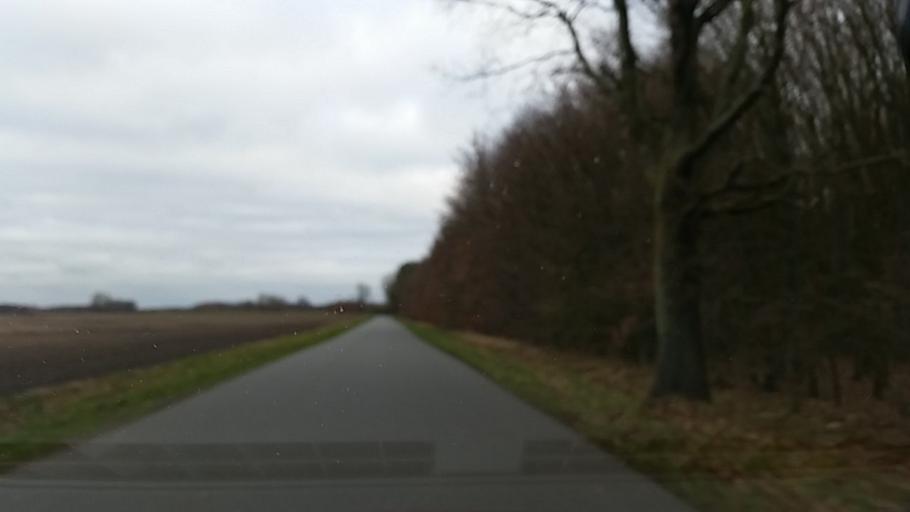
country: DE
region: Lower Saxony
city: Luder
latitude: 52.8178
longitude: 10.6691
